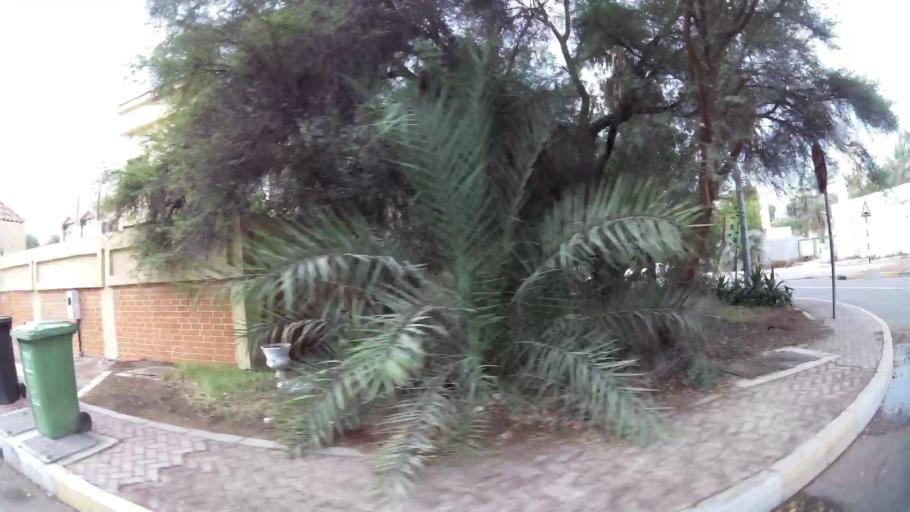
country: AE
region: Abu Dhabi
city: Abu Dhabi
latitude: 24.4419
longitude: 54.3941
